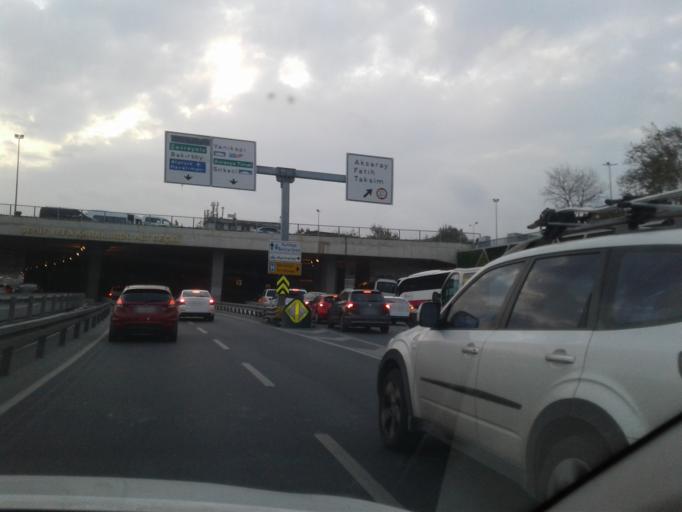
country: TR
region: Istanbul
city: Istanbul
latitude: 41.0036
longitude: 28.9550
